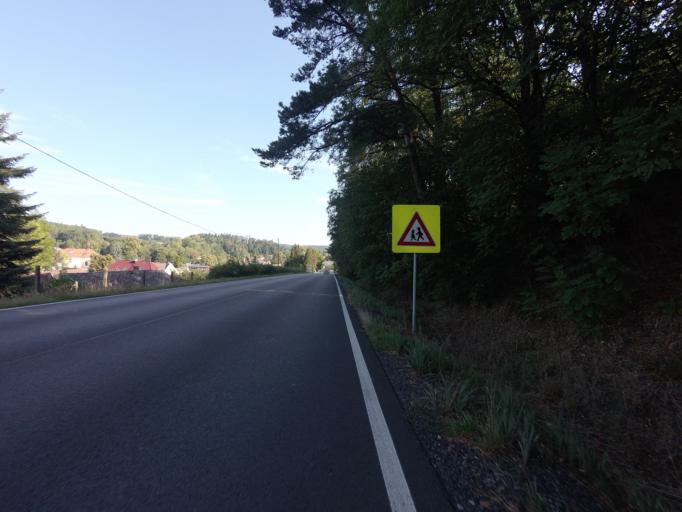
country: CZ
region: Jihocesky
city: Tyn nad Vltavou
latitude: 49.2505
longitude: 14.4213
